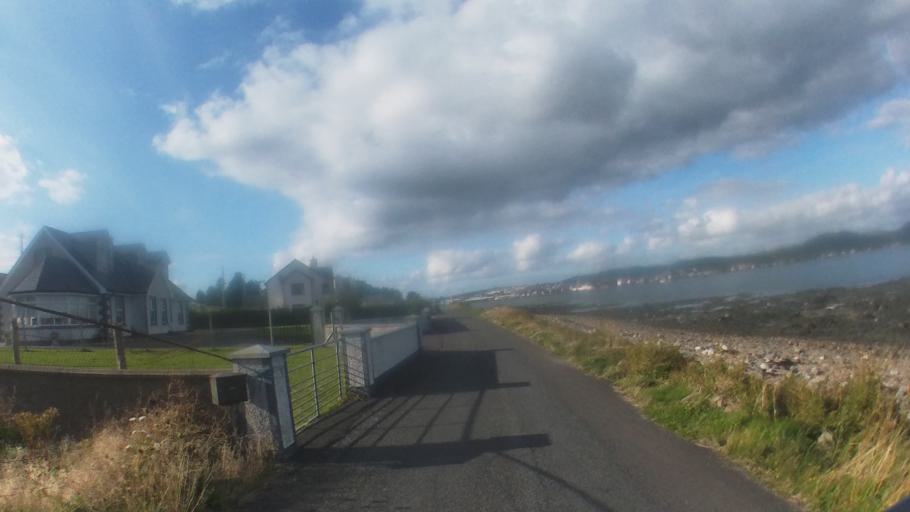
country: GB
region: Northern Ireland
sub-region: Down District
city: Warrenpoint
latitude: 54.0611
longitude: -6.2745
